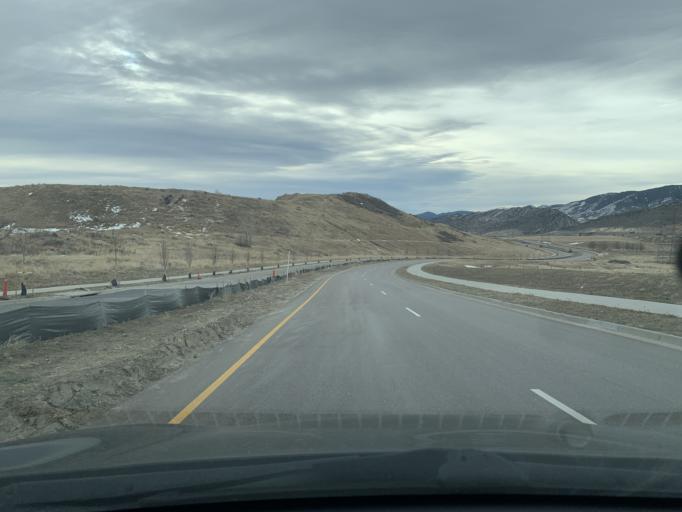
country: US
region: Colorado
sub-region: Jefferson County
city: West Pleasant View
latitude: 39.6833
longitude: -105.1833
